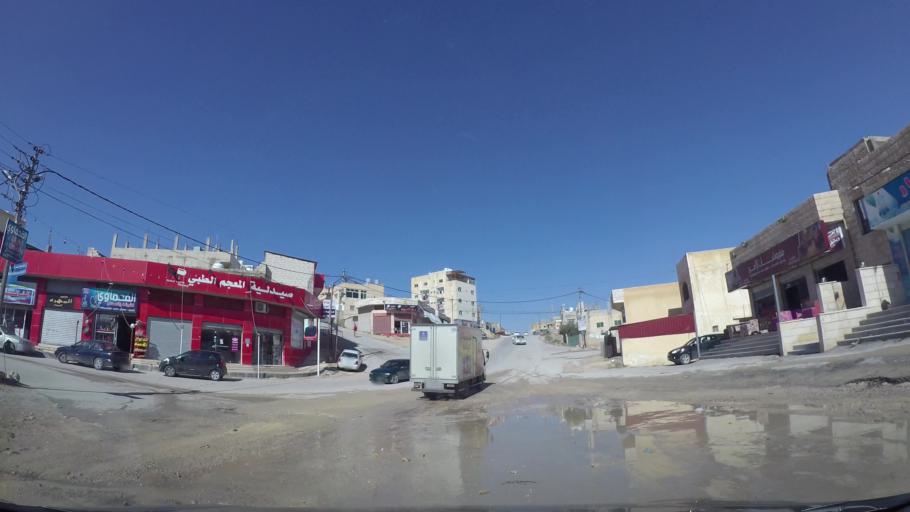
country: JO
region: Zarqa
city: Russeifa
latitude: 32.0392
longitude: 36.0516
